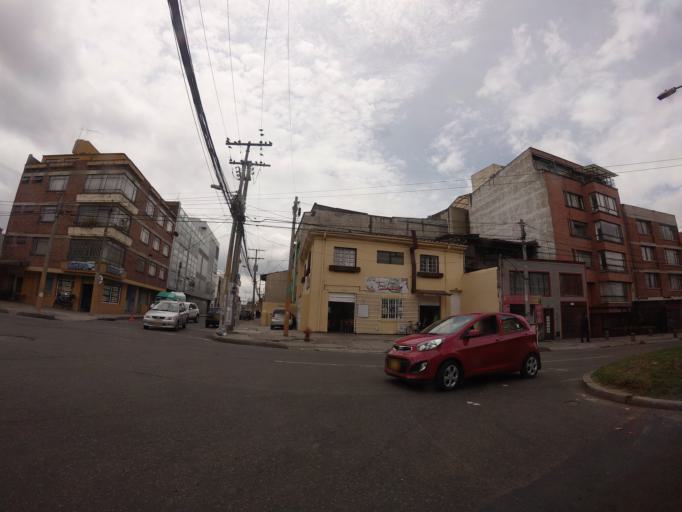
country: CO
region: Bogota D.C.
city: Bogota
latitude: 4.6222
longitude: -74.0757
